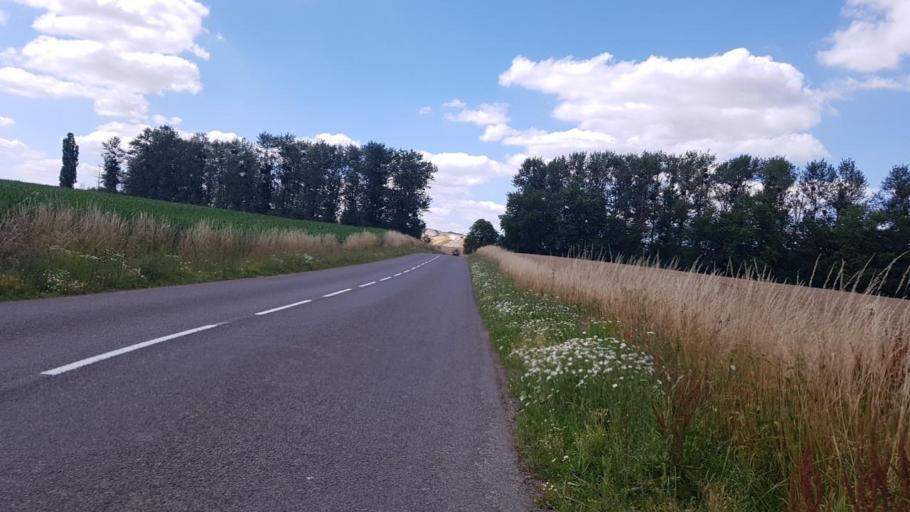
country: FR
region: Ile-de-France
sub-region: Departement de Seine-et-Marne
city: Longperrier
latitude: 49.0176
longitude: 2.6512
